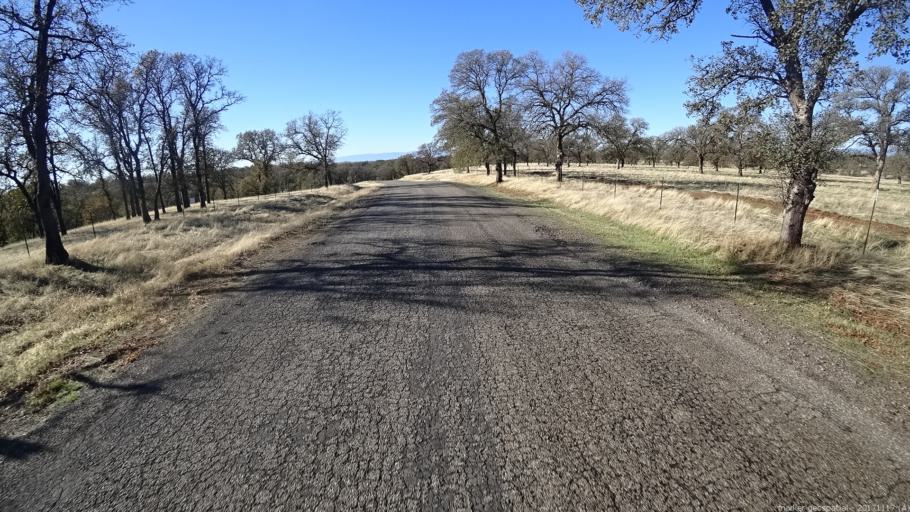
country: US
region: California
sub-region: Shasta County
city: Cottonwood
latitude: 40.4240
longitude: -122.1866
